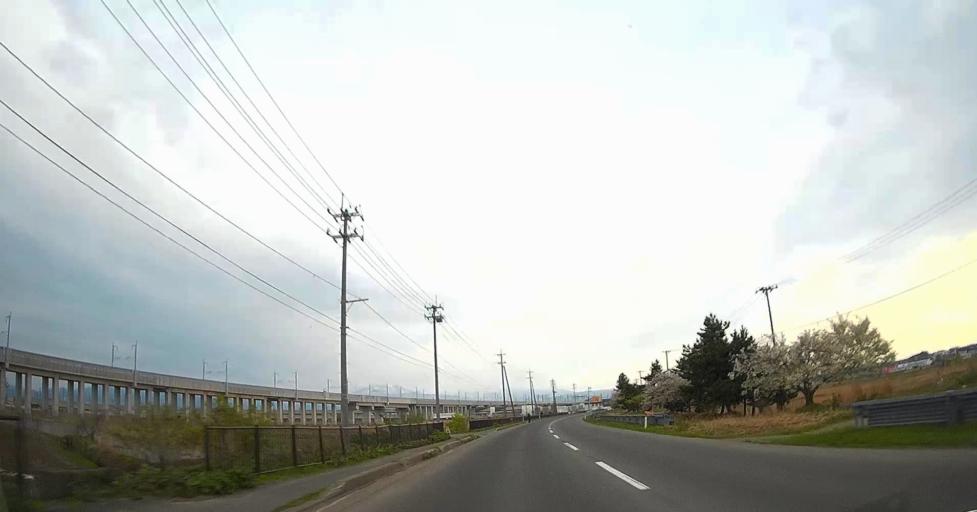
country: JP
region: Aomori
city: Aomori Shi
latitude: 40.8409
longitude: 140.6899
